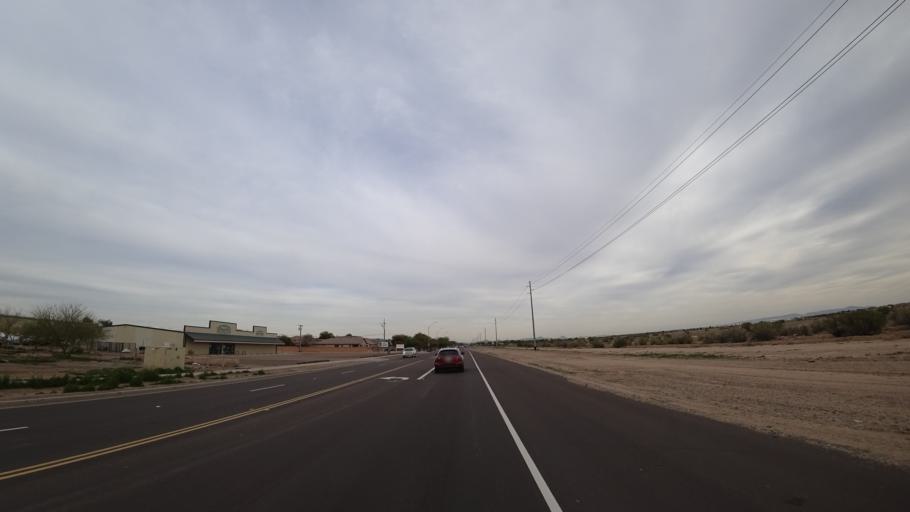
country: US
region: Arizona
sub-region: Maricopa County
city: Surprise
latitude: 33.6092
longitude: -112.3694
